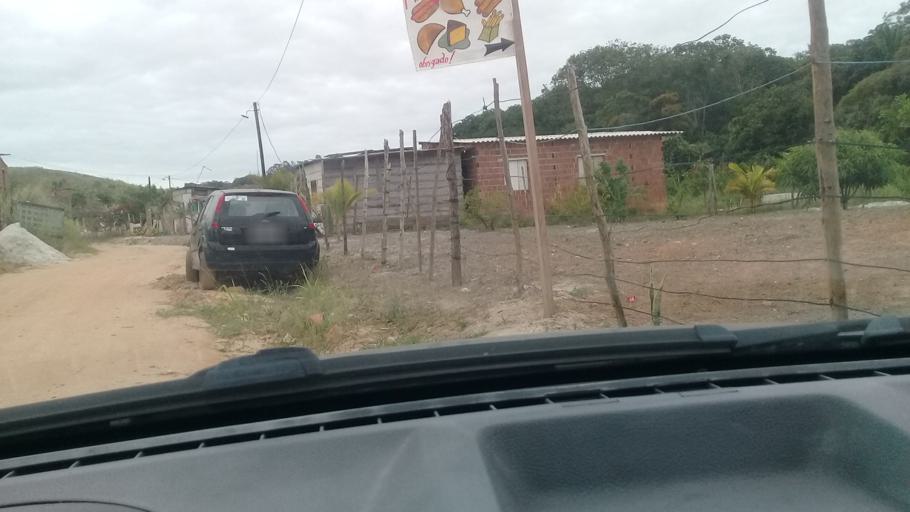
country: BR
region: Pernambuco
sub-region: Jaboatao Dos Guararapes
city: Jaboatao dos Guararapes
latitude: -8.0811
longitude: -35.0362
